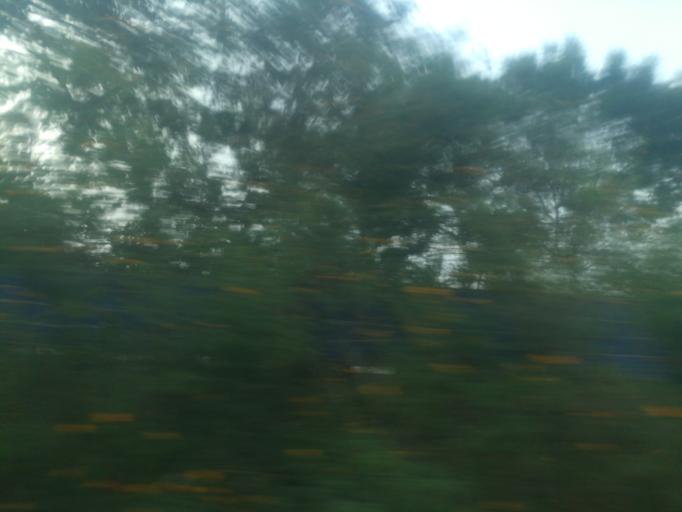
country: NG
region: Ogun
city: Abeokuta
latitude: 7.1623
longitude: 3.2670
